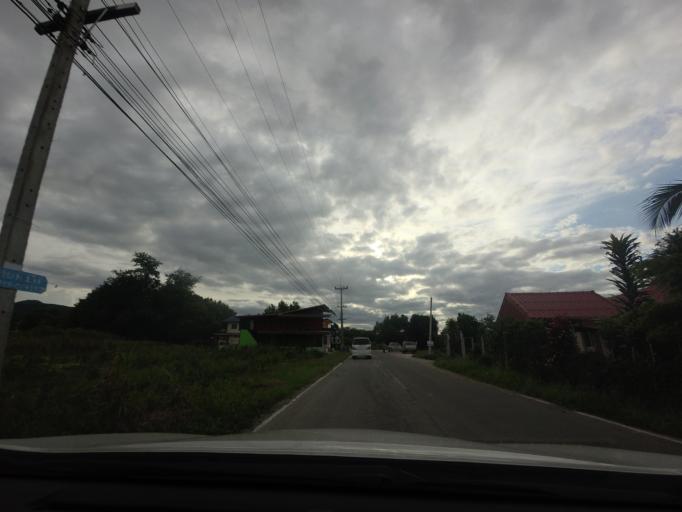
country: TH
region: Nakhon Ratchasima
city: Pak Chong
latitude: 14.6069
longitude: 101.4380
